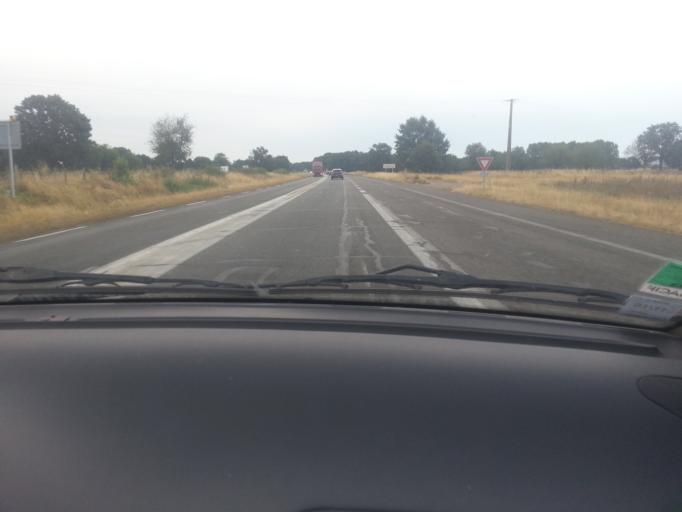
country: FR
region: Bourgogne
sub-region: Departement de Saone-et-Loire
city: Paray-le-Monial
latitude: 46.4786
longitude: 4.1434
